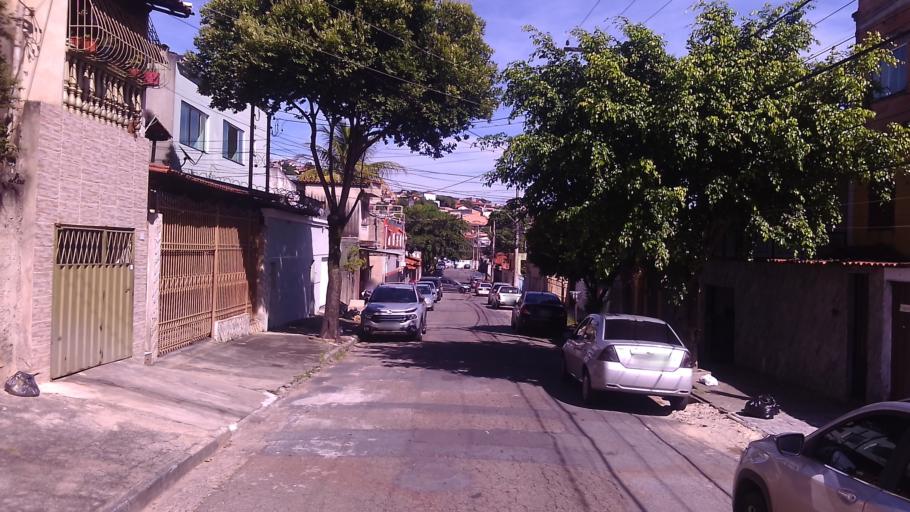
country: BR
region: Minas Gerais
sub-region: Contagem
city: Contagem
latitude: -19.9071
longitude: -44.0047
